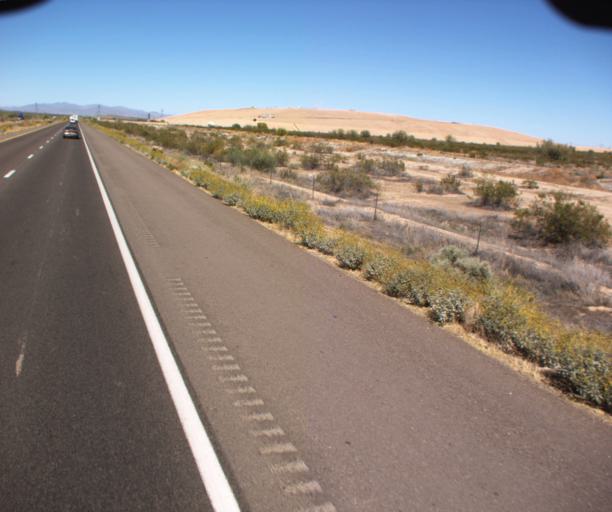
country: US
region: Arizona
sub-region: Maricopa County
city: Buckeye
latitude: 33.2128
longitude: -112.6452
